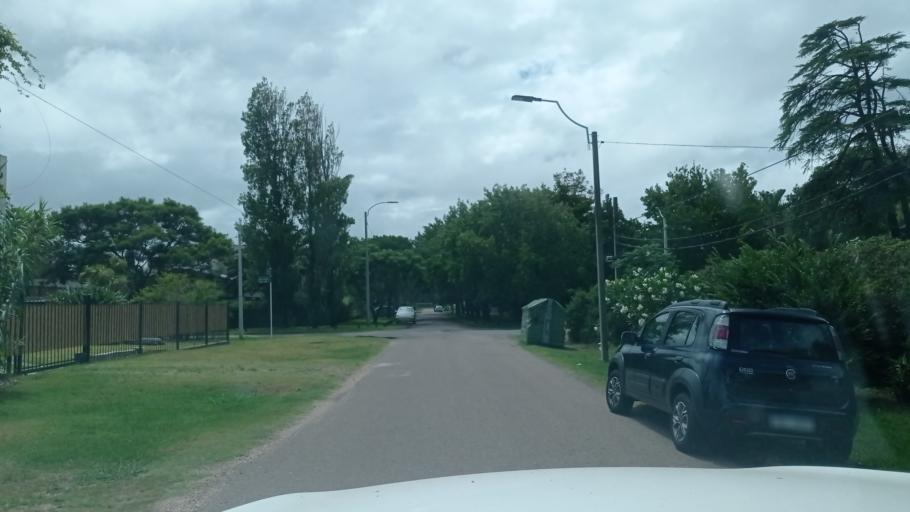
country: UY
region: Canelones
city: Barra de Carrasco
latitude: -34.8843
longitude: -56.0447
